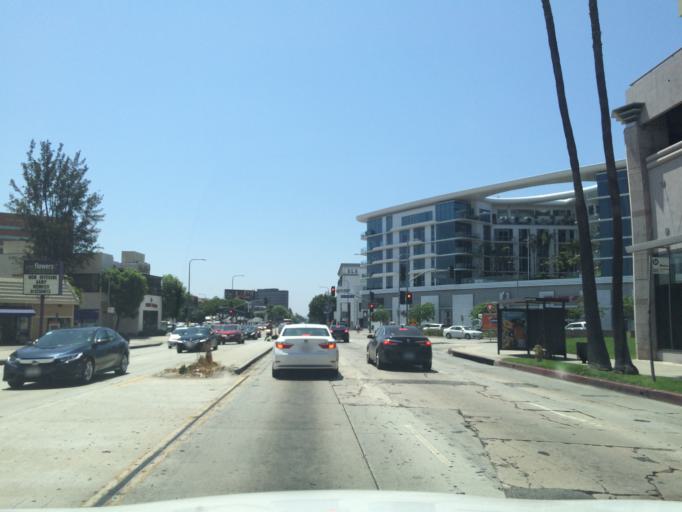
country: US
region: California
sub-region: Los Angeles County
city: West Hollywood
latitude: 34.0723
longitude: -118.3765
